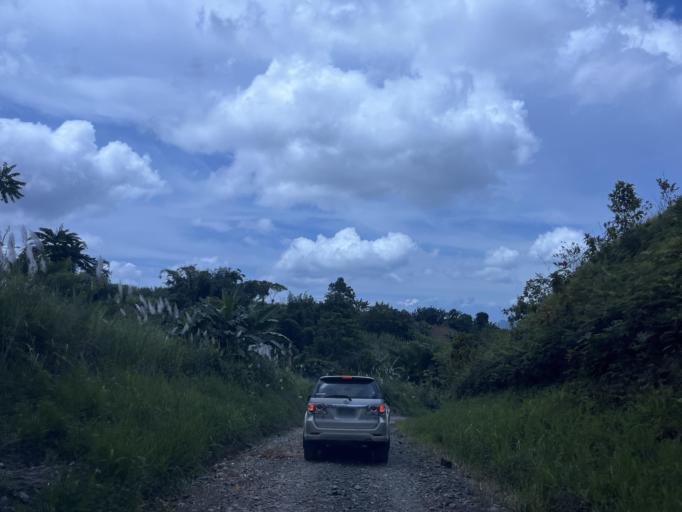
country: PH
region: Northern Mindanao
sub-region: Province of Bukidnon
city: Sumilao
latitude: 8.2995
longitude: 124.9296
